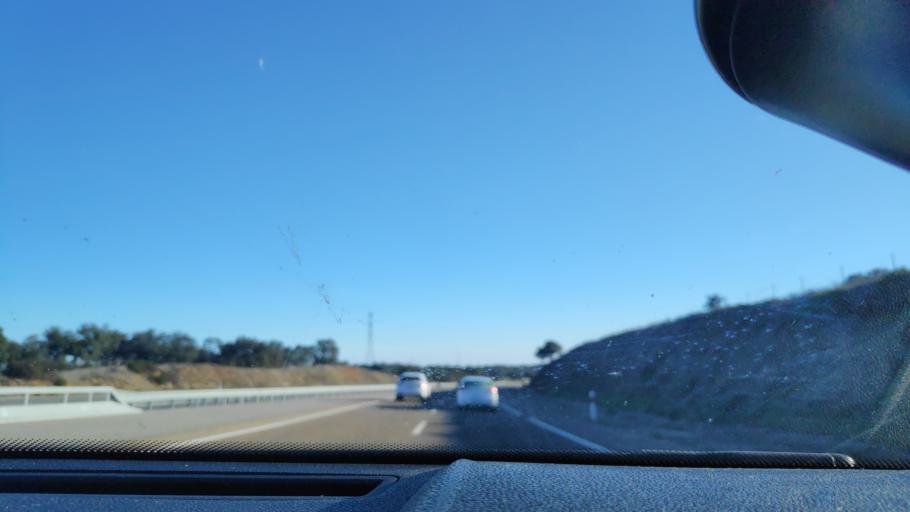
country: ES
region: Andalusia
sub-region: Provincia de Sevilla
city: Gerena
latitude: 37.6177
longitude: -6.1270
